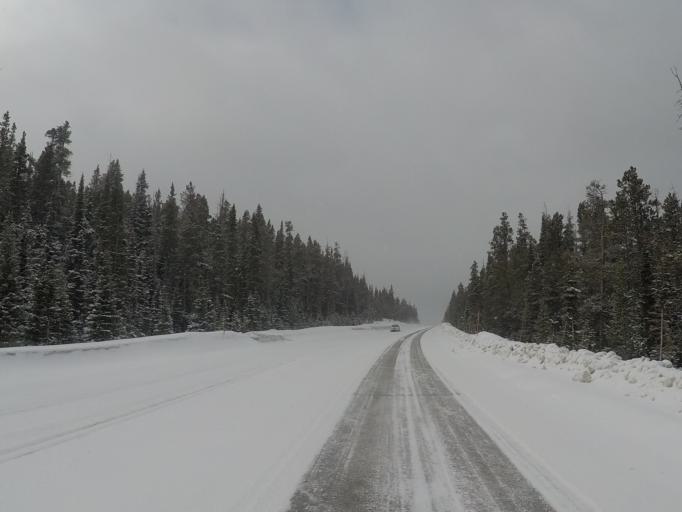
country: US
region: Montana
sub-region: Meagher County
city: White Sulphur Springs
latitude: 46.8469
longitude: -110.6905
